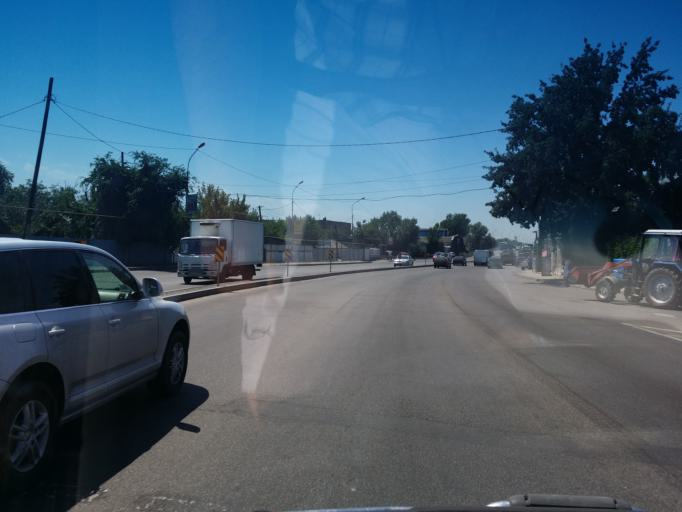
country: KZ
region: Almaty Qalasy
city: Almaty
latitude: 43.2820
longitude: 76.9157
